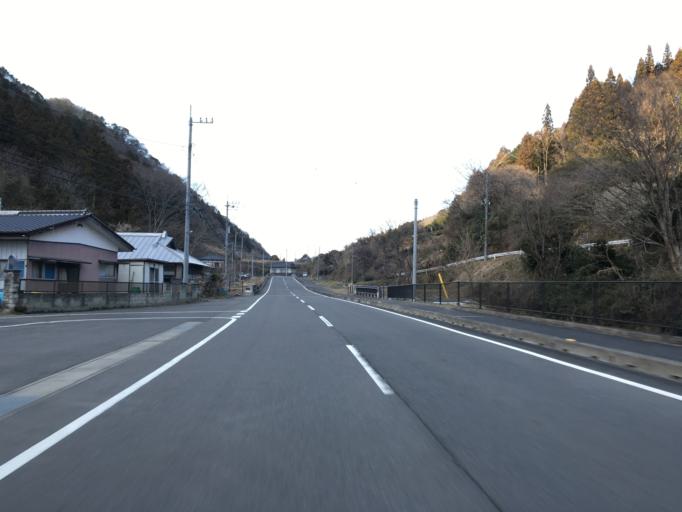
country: JP
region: Ibaraki
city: Daigo
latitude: 36.7172
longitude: 140.4628
